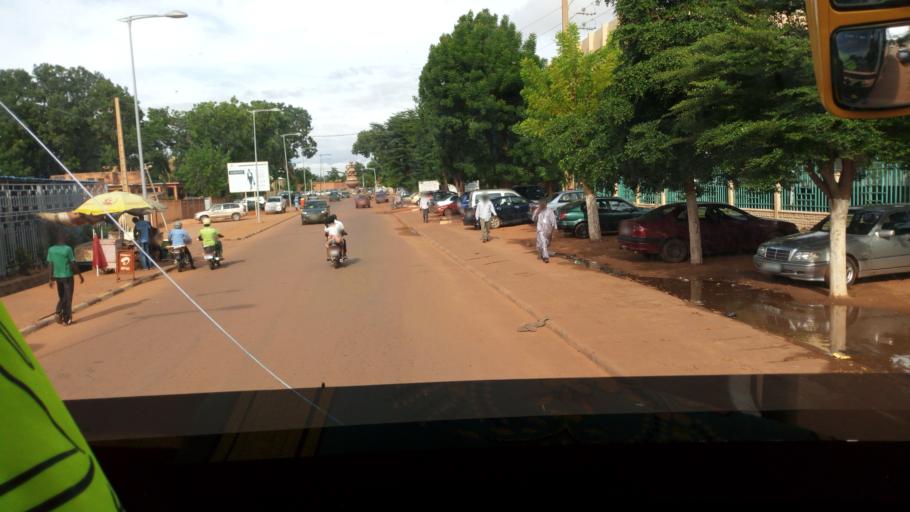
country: NE
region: Niamey
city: Niamey
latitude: 13.5157
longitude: 2.1030
